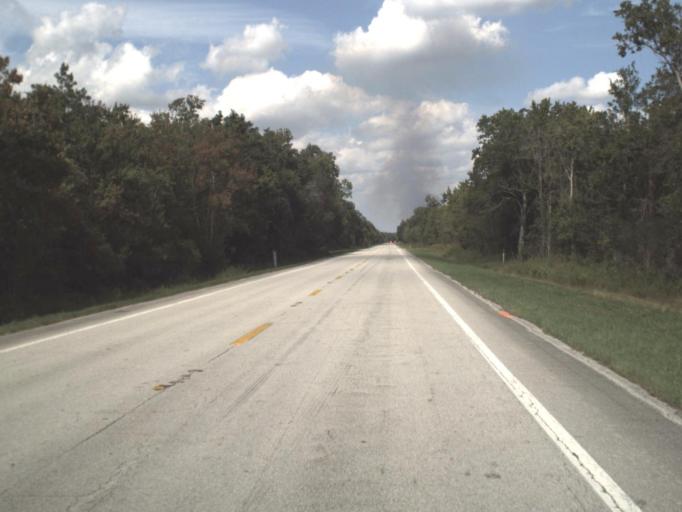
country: US
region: Florida
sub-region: Okeechobee County
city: Cypress Quarters
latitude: 27.5039
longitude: -80.8063
